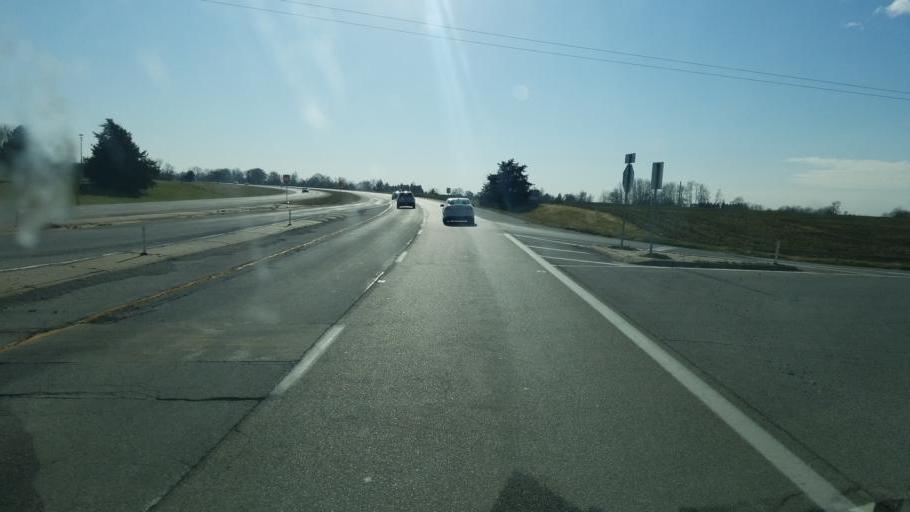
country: US
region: Illinois
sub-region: Warren County
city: Monmouth
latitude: 40.9215
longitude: -90.6623
